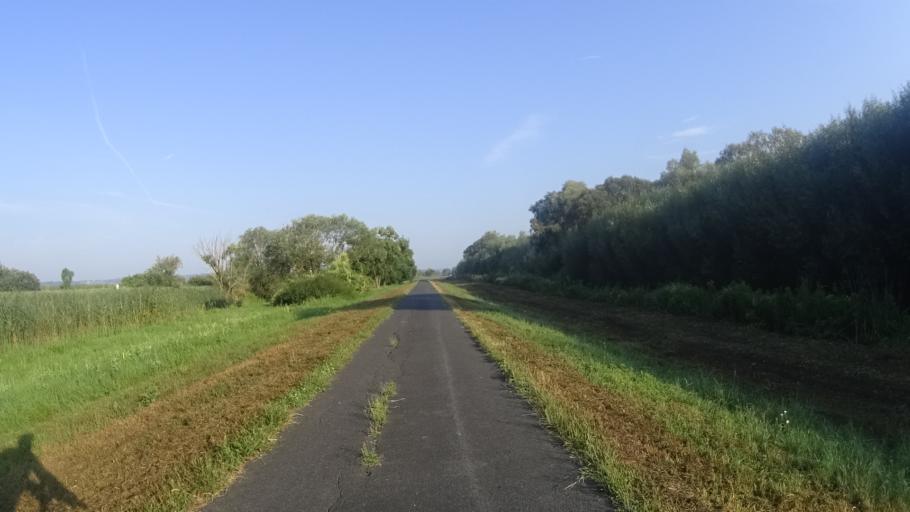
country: HU
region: Zala
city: Sarmellek
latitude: 46.6385
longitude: 17.1680
